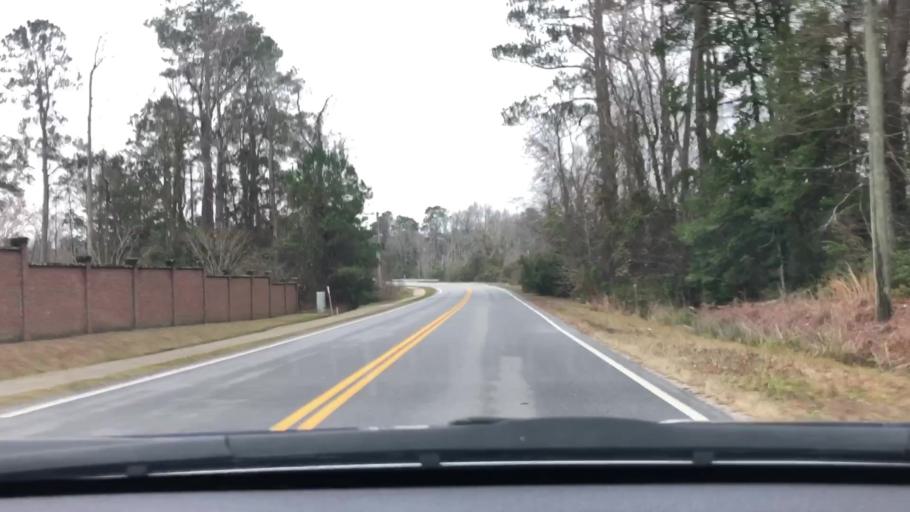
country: US
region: South Carolina
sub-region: Sumter County
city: Cherryvale
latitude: 33.9491
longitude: -80.4027
